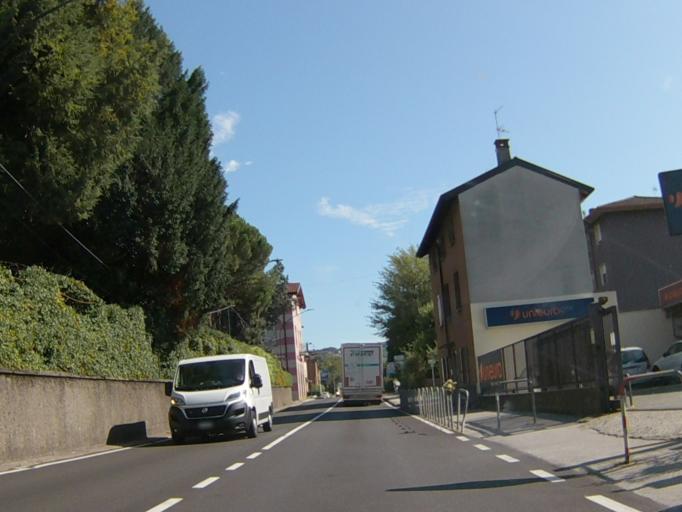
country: IT
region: Lombardy
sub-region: Provincia di Lecco
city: Calolziocorte
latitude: 45.7955
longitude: 9.4357
